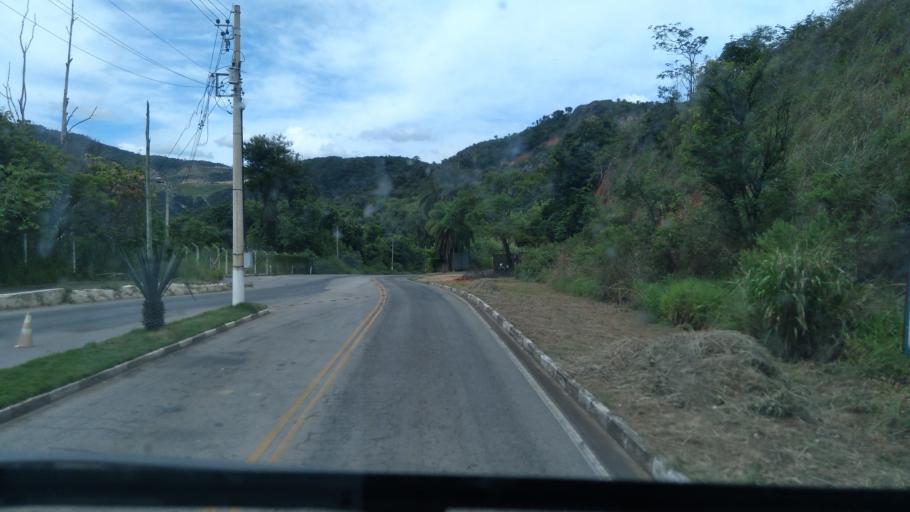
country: BR
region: Minas Gerais
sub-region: Belo Horizonte
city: Belo Horizonte
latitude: -19.8709
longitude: -43.8557
